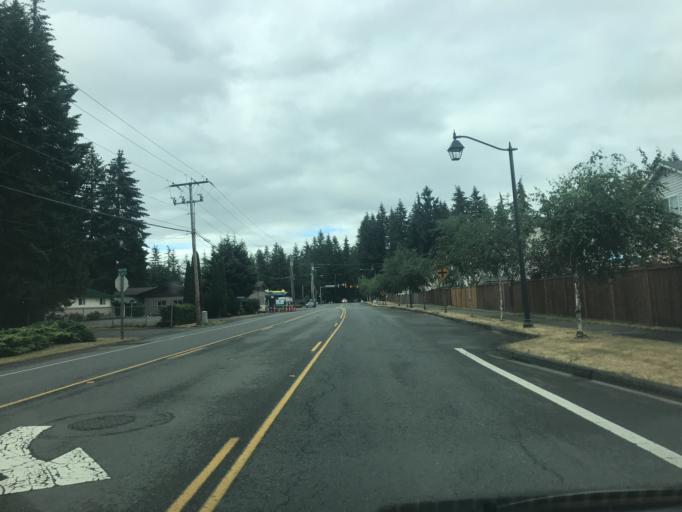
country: US
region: Washington
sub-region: King County
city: Lake Morton-Berrydale
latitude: 47.3426
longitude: -122.0540
